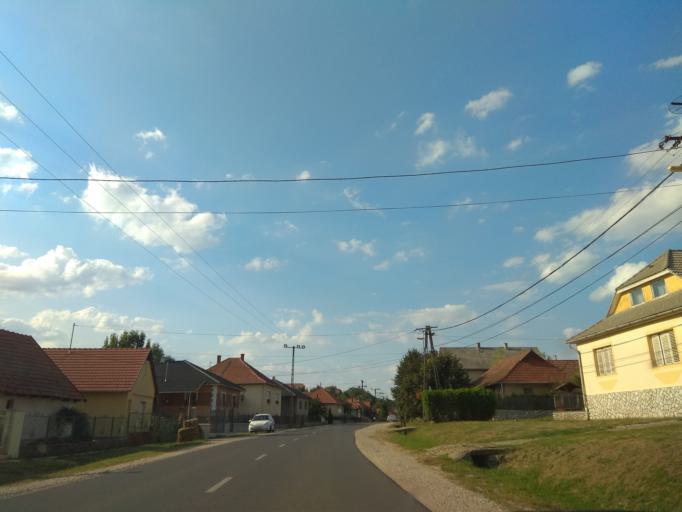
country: HU
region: Borsod-Abauj-Zemplen
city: Harsany
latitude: 47.9680
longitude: 20.7409
